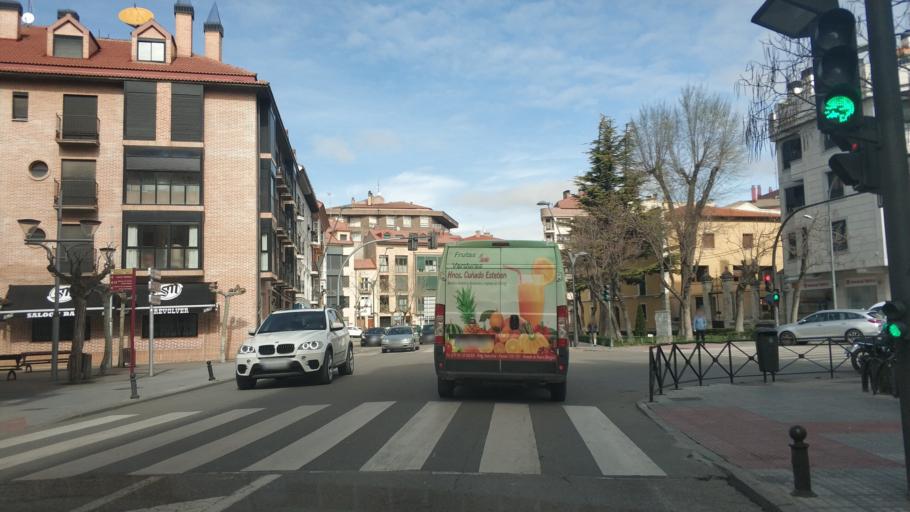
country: ES
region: Castille and Leon
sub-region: Provincia de Burgos
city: Aranda de Duero
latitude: 41.6727
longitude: -3.6855
